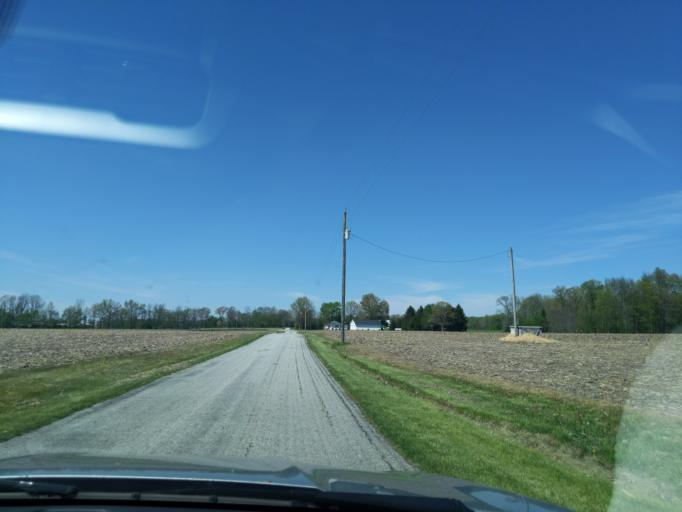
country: US
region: Indiana
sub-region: Decatur County
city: Greensburg
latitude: 39.2460
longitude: -85.4334
